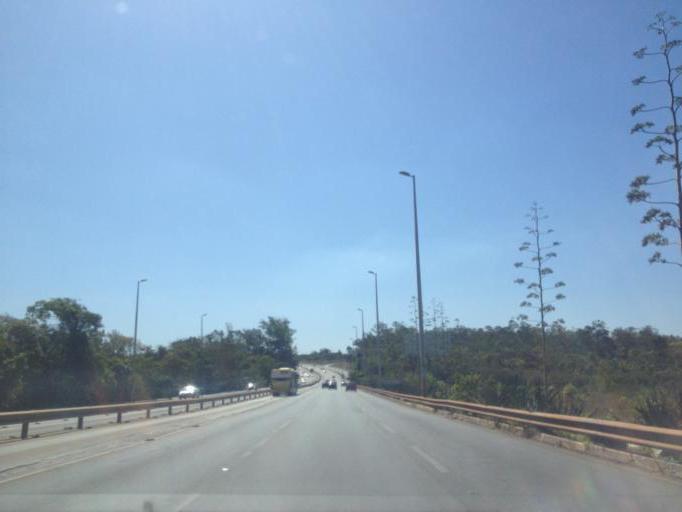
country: BR
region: Federal District
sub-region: Brasilia
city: Brasilia
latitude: -15.8540
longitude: -47.9330
